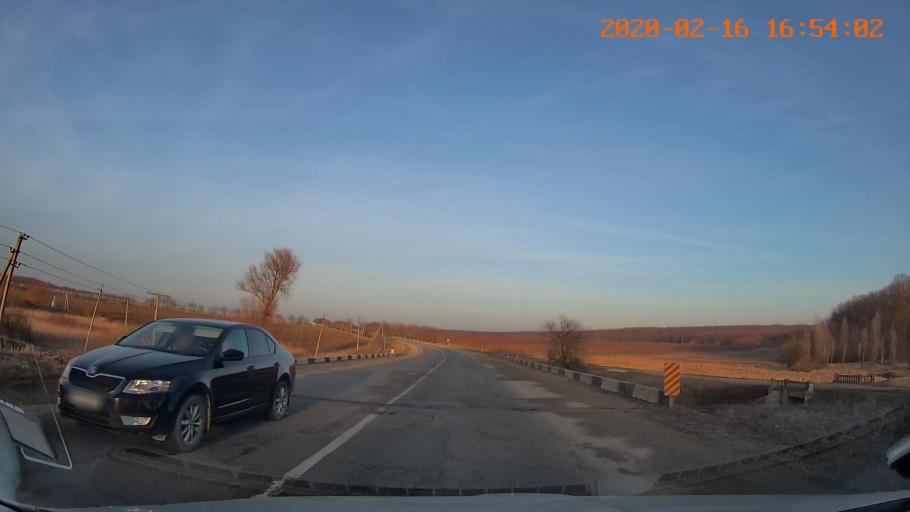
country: MD
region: Briceni
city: Briceni
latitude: 48.3169
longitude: 26.9987
